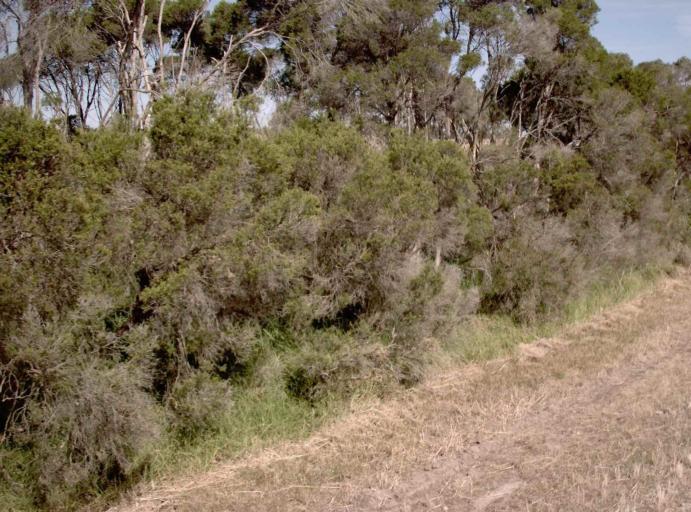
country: AU
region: Victoria
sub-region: Wellington
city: Sale
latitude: -38.3184
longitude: 147.1565
